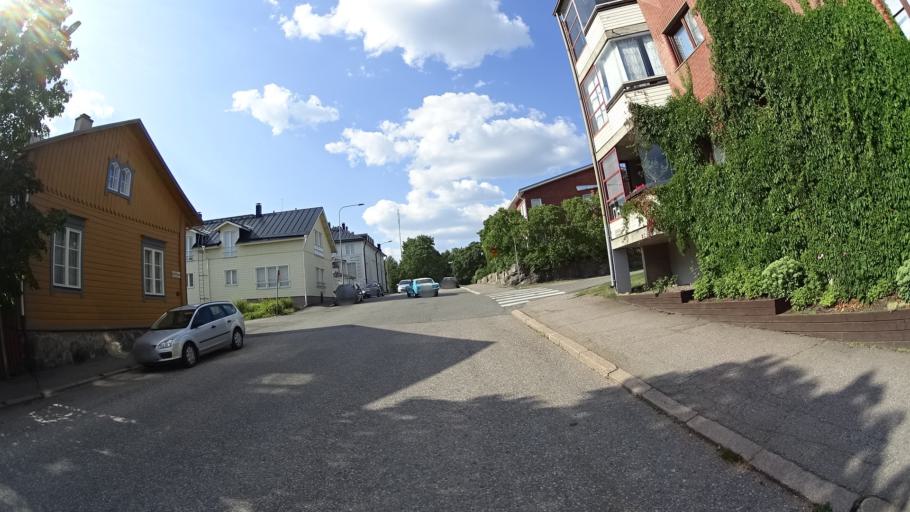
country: FI
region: Uusimaa
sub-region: Porvoo
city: Porvoo
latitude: 60.3985
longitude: 25.6624
